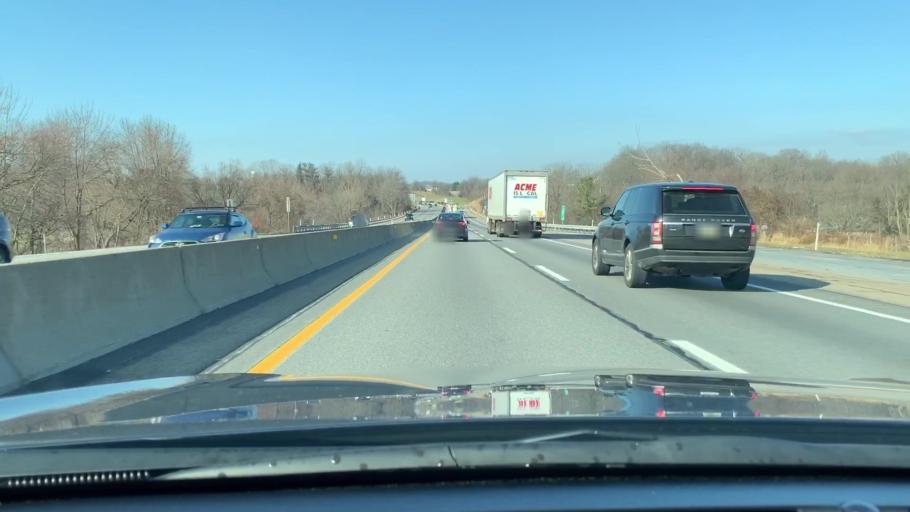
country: US
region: Pennsylvania
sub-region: Chester County
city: Downingtown
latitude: 40.0797
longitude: -75.7042
